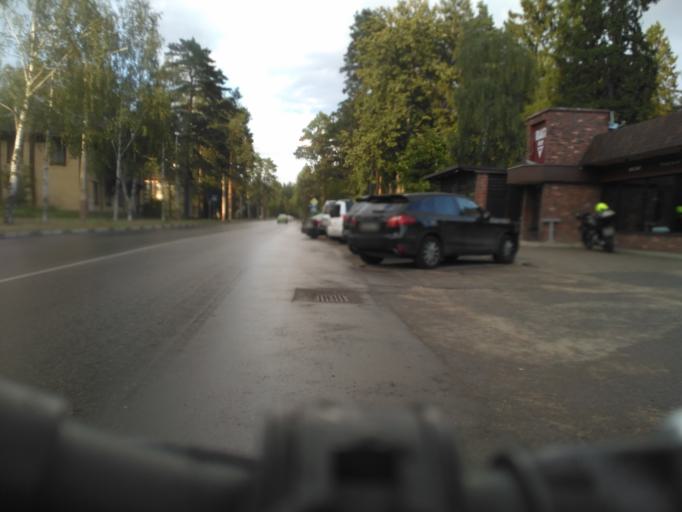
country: RU
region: Moskovskaya
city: Dubna
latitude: 56.7404
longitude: 37.1736
